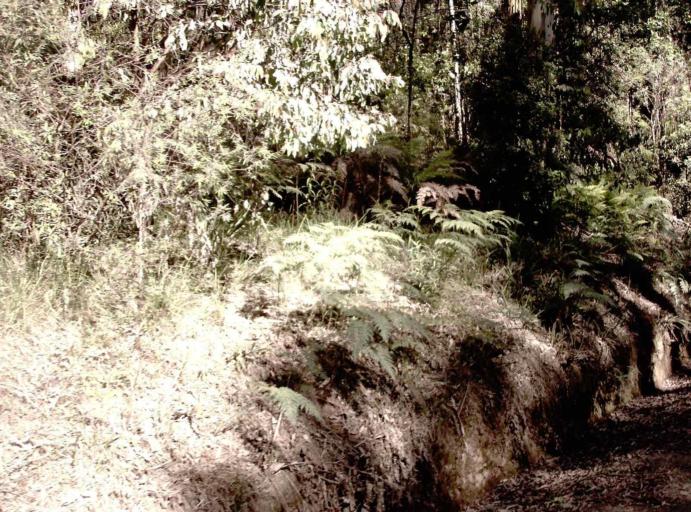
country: AU
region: New South Wales
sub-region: Bombala
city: Bombala
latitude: -37.2322
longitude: 148.7536
